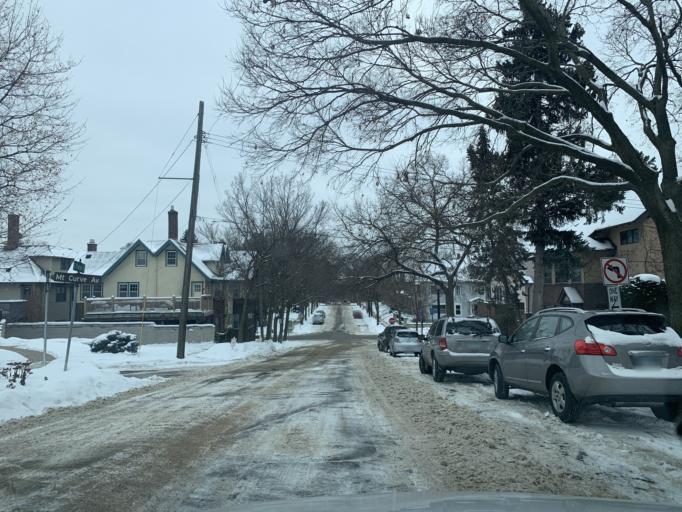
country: US
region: Minnesota
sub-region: Hennepin County
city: Minneapolis
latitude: 44.9671
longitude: -93.2956
